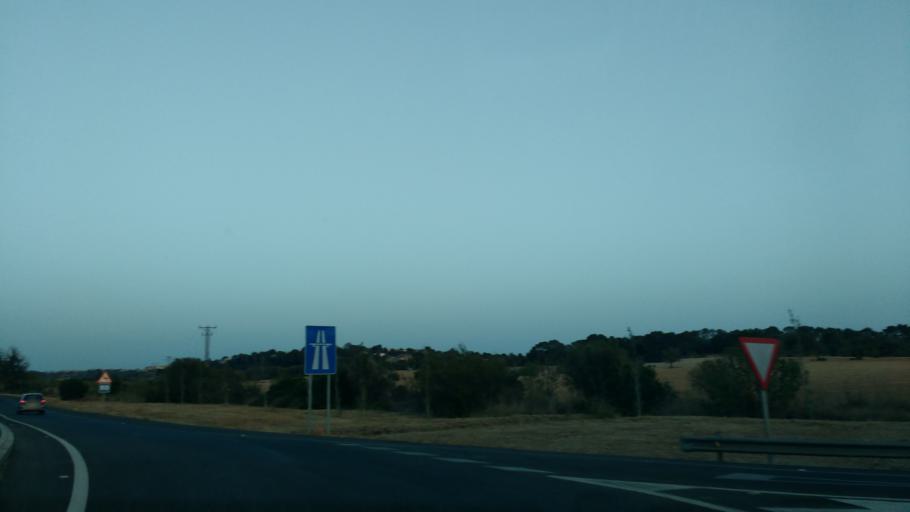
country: ES
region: Balearic Islands
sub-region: Illes Balears
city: Marratxi
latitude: 39.6295
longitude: 2.7360
